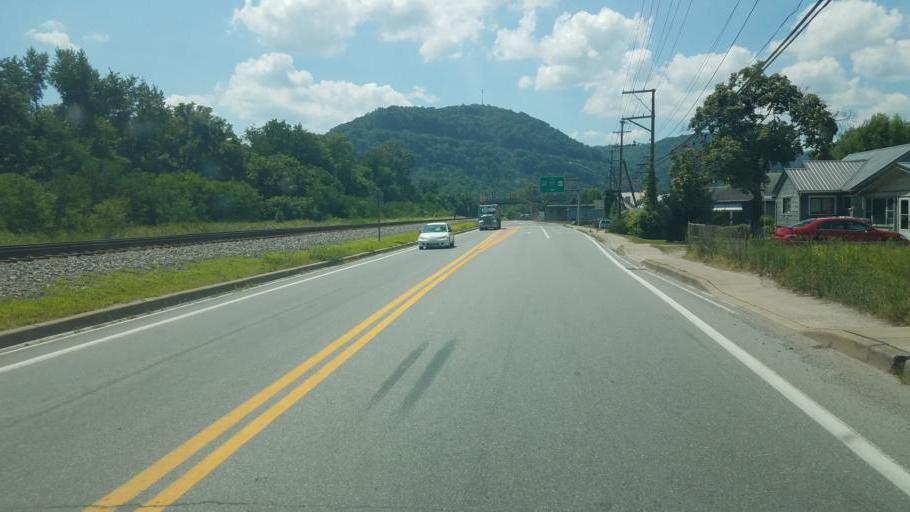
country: US
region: West Virginia
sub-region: Kanawha County
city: Chesapeake
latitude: 38.1952
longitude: -81.4914
